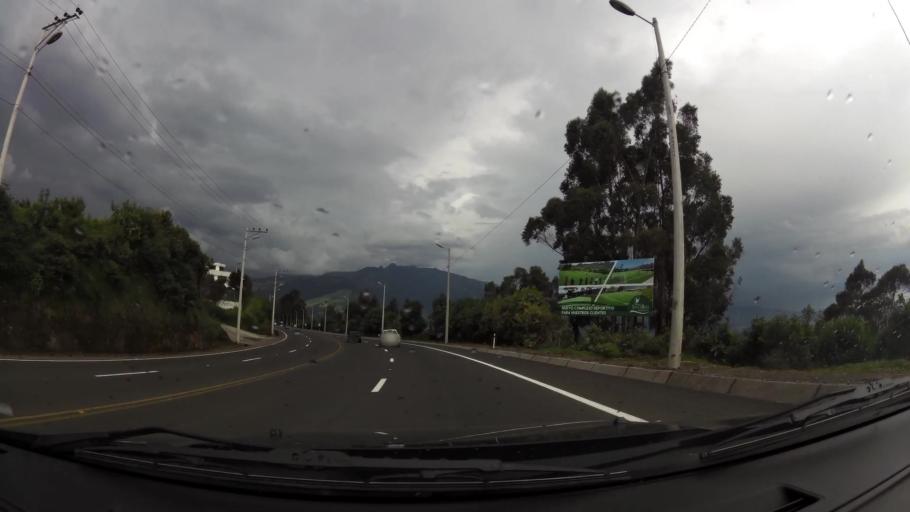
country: EC
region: Pichincha
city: Sangolqui
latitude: -0.3885
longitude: -78.5491
